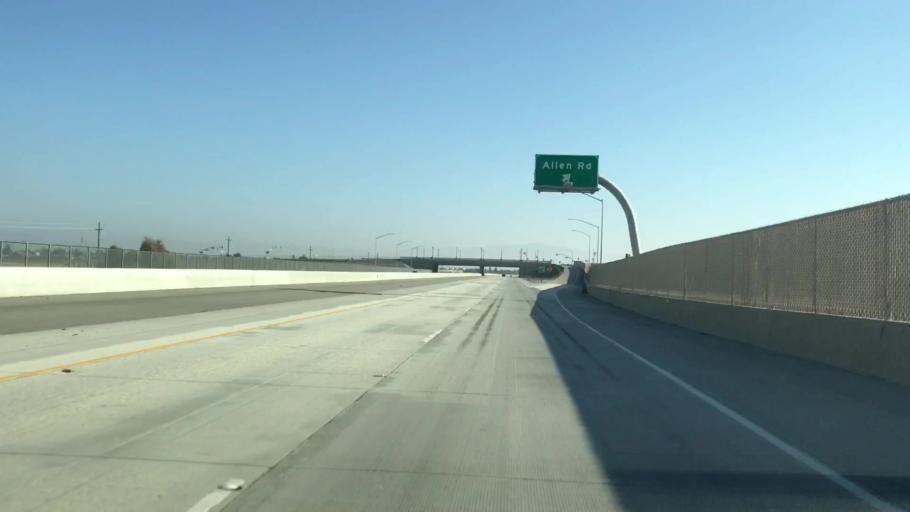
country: US
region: California
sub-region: Kern County
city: Rosedale
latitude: 35.3598
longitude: -119.1507
